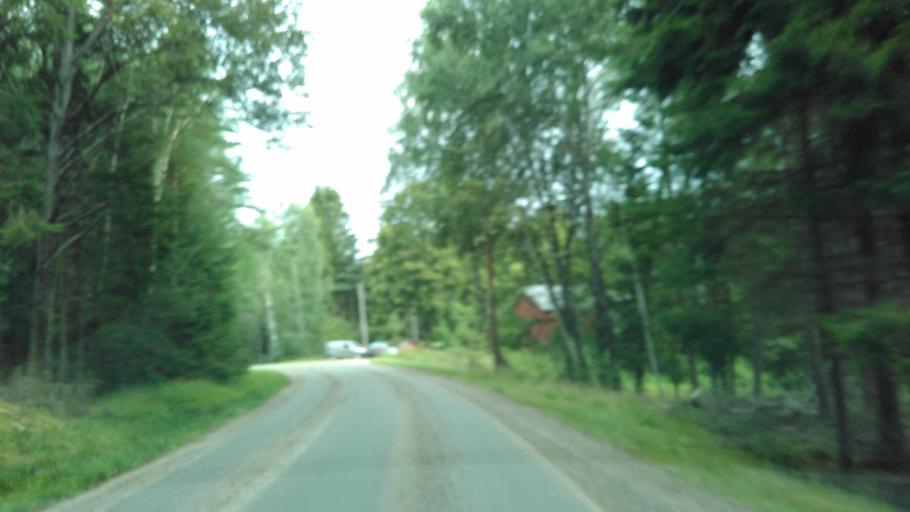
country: SE
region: Vaestra Goetaland
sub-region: Marks Kommun
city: Fritsla
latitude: 57.5742
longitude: 12.7703
